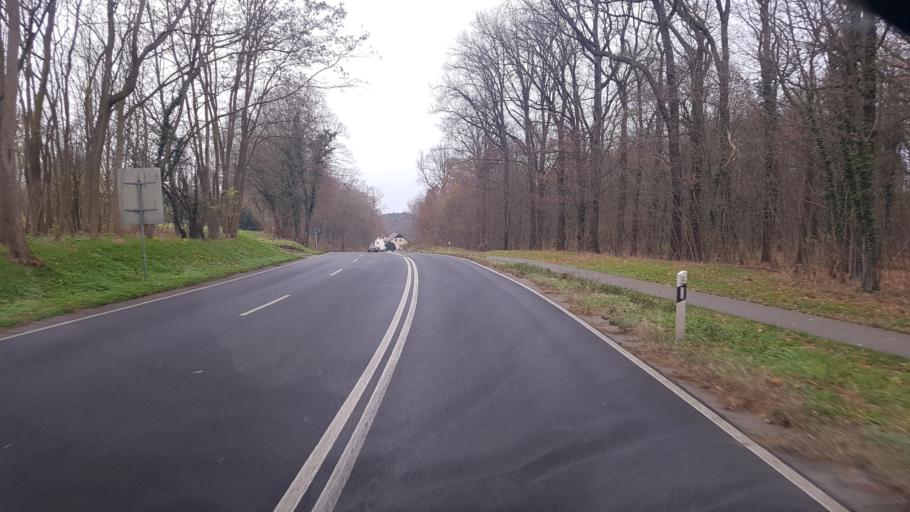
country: DE
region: Brandenburg
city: Neuzelle
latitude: 52.0813
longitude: 14.6582
